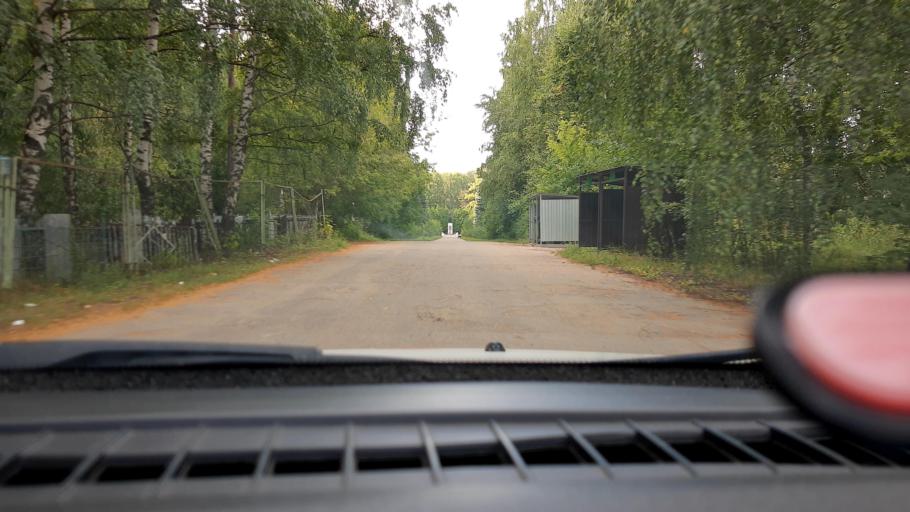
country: RU
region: Nizjnij Novgorod
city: Nizhniy Novgorod
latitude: 56.2830
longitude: 43.8881
